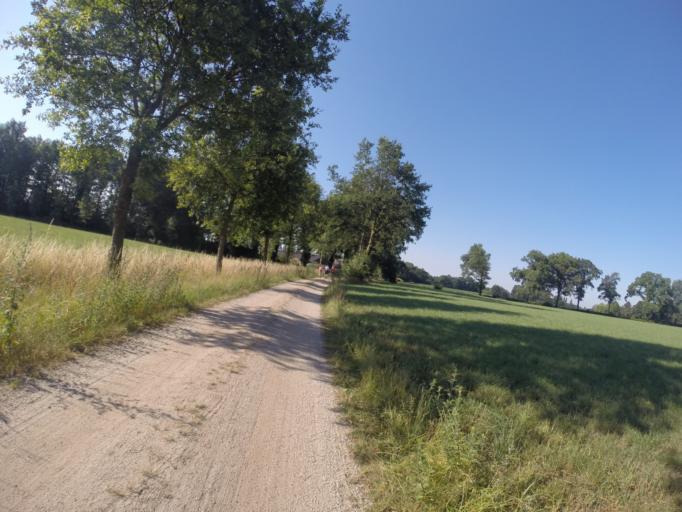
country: NL
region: Gelderland
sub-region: Gemeente Bronckhorst
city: Hengelo
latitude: 52.0841
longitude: 6.3533
